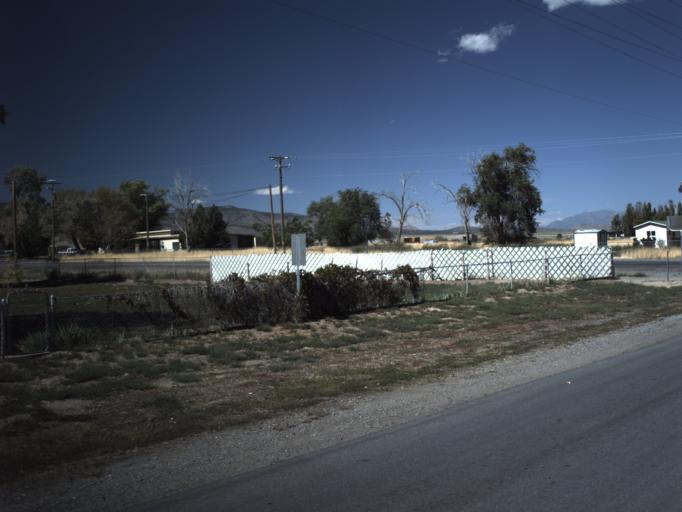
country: US
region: Utah
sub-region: Utah County
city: Genola
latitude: 39.9515
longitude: -111.9561
